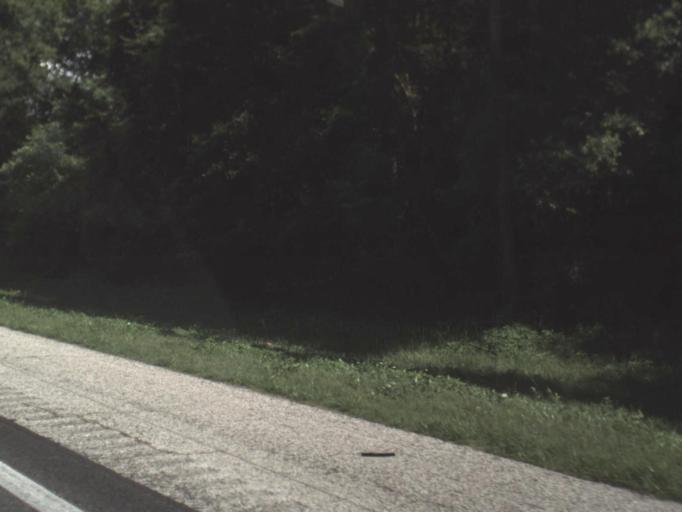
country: US
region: Florida
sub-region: Alachua County
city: Alachua
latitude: 29.7557
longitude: -82.4960
